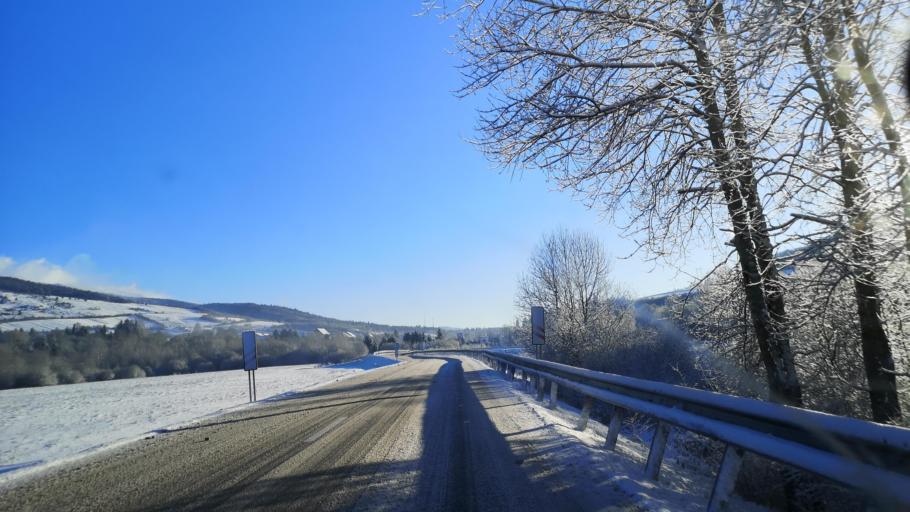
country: SK
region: Banskobystricky
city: Tisovec
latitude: 48.8521
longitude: 20.0033
